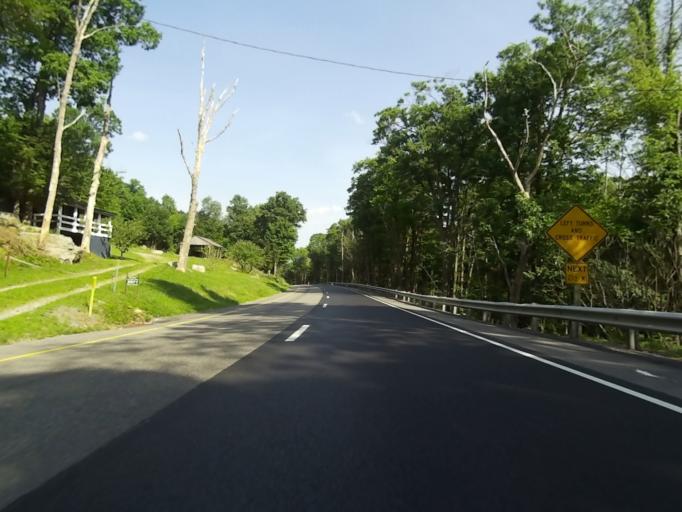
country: US
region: Pennsylvania
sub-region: Centre County
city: Stormstown
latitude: 40.8273
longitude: -78.1118
